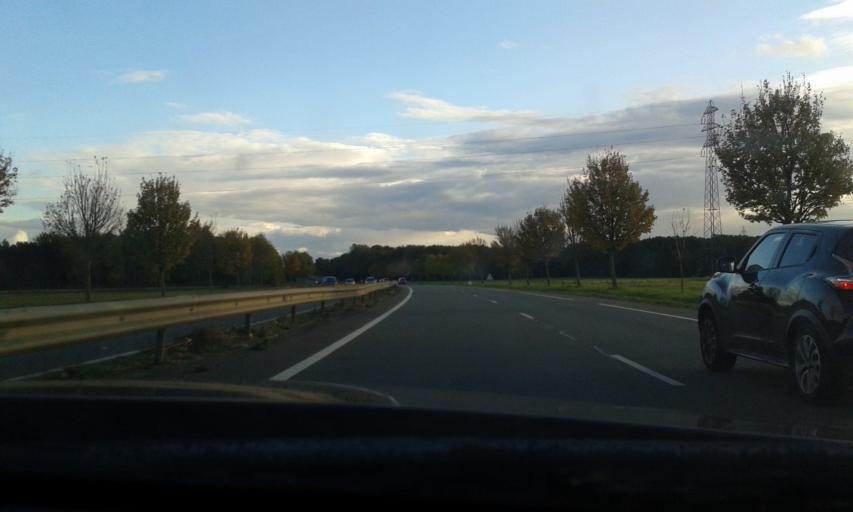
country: FR
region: Centre
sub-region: Departement d'Eure-et-Loir
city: Mainvilliers
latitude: 48.4316
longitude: 1.4313
